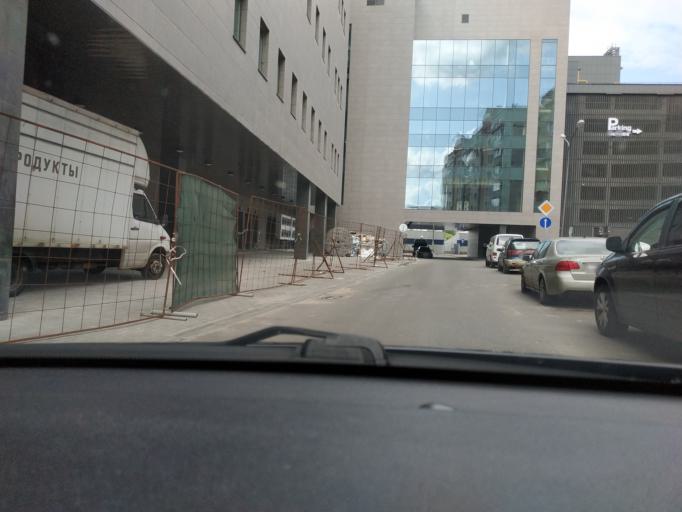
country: BY
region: Mogilev
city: Mahilyow
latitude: 53.9038
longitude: 30.3396
